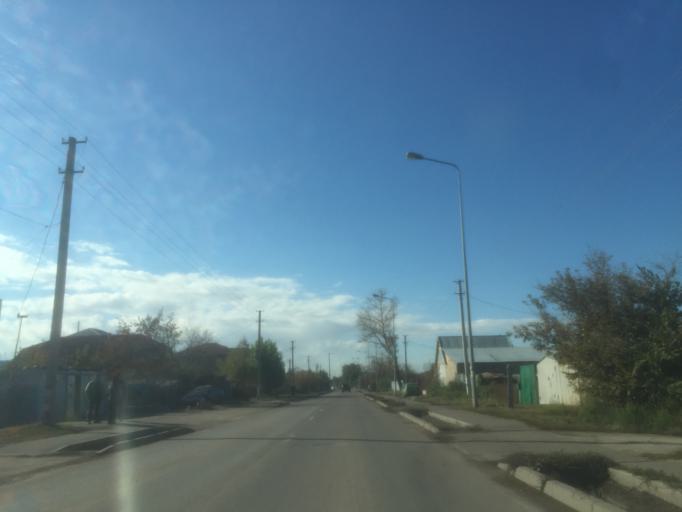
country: KZ
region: Astana Qalasy
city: Astana
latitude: 51.2007
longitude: 71.3703
